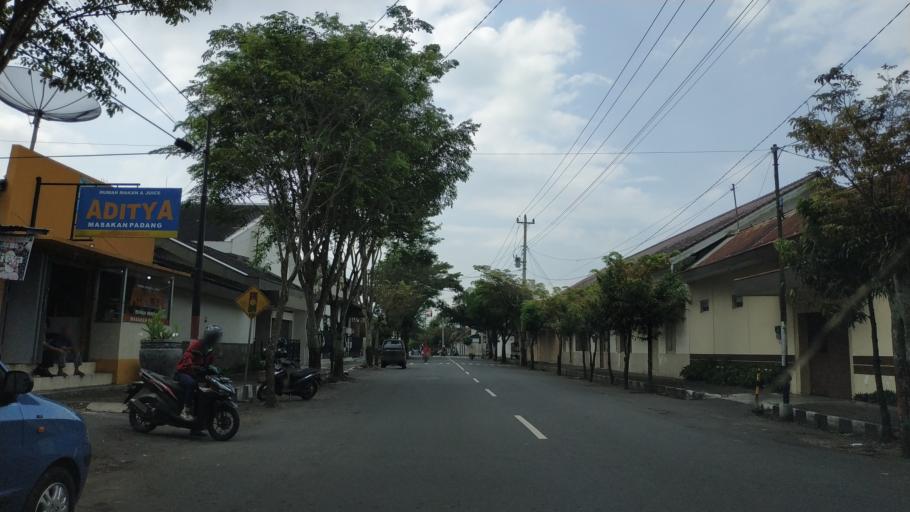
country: ID
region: Central Java
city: Magelang
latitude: -7.3145
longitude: 110.1772
